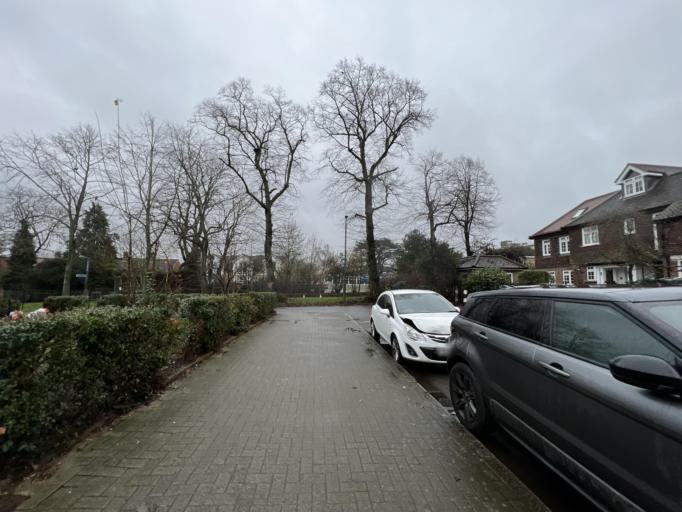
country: GB
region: England
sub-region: Greater London
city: Wandsworth
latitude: 51.4559
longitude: -0.2344
